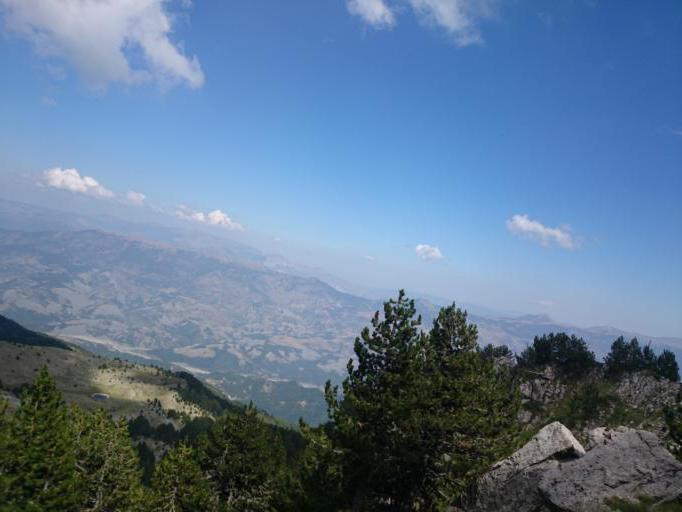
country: AL
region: Berat
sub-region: Rrethi i Beratit
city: Polican
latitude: 40.6577
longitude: 20.1588
